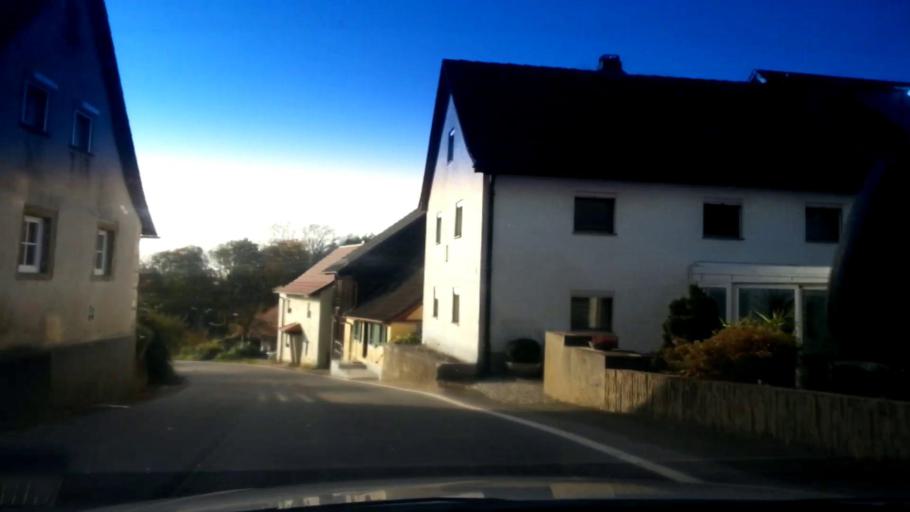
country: DE
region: Bavaria
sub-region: Upper Franconia
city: Poxdorf
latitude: 49.9518
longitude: 11.0858
